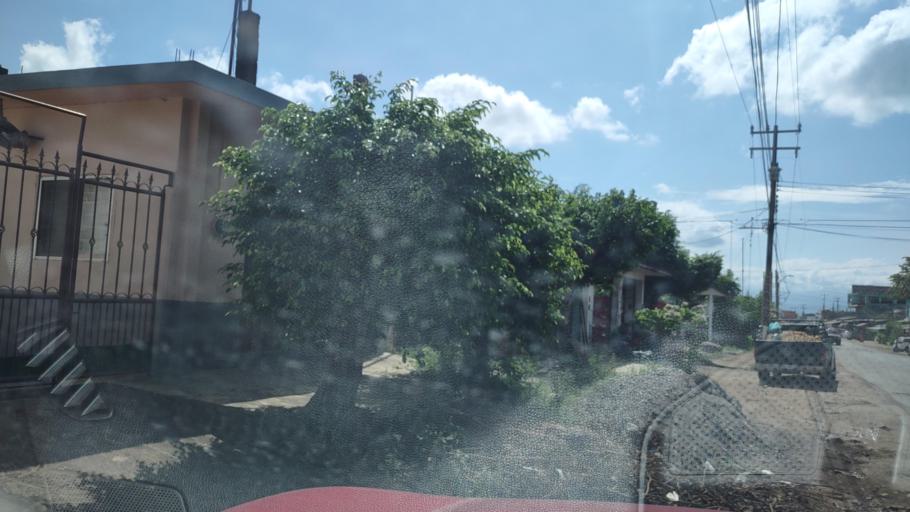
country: MX
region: Veracruz
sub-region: Martinez de la Torre
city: La Union Paso Largo
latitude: 20.1309
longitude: -96.9967
